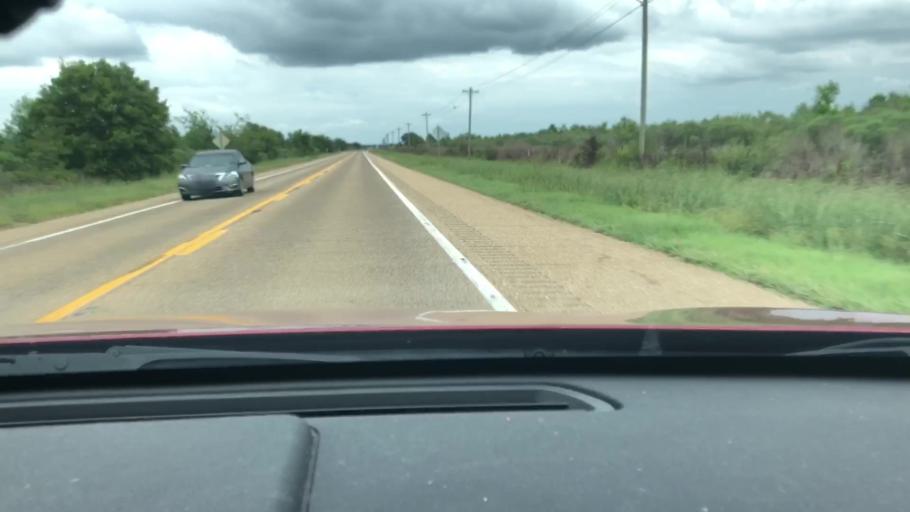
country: US
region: Arkansas
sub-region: Lafayette County
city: Lewisville
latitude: 33.4126
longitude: -93.8043
